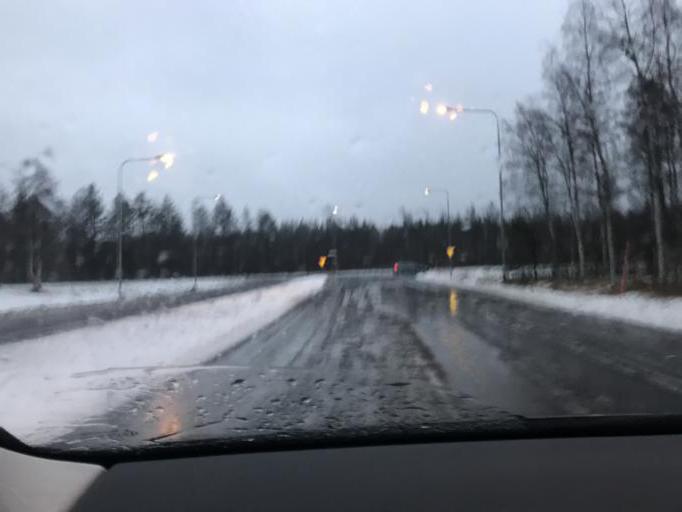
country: SE
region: Norrbotten
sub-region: Lulea Kommun
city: Sodra Sunderbyn
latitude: 65.6548
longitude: 21.9677
